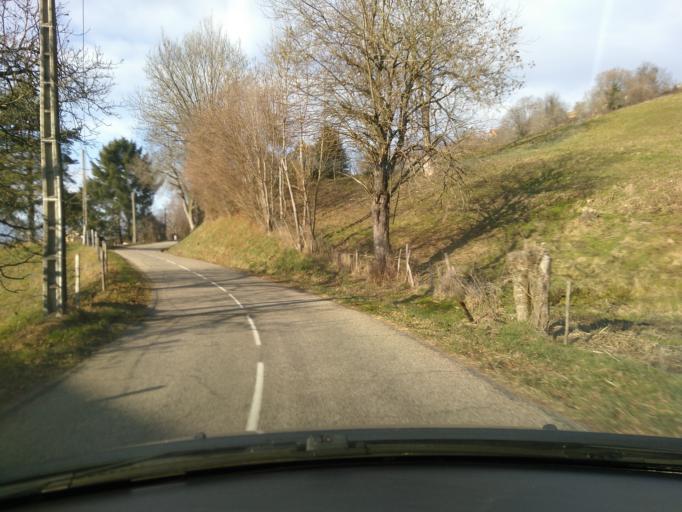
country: FR
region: Rhone-Alpes
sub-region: Departement de l'Isere
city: Froges
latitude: 45.2318
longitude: 5.9343
